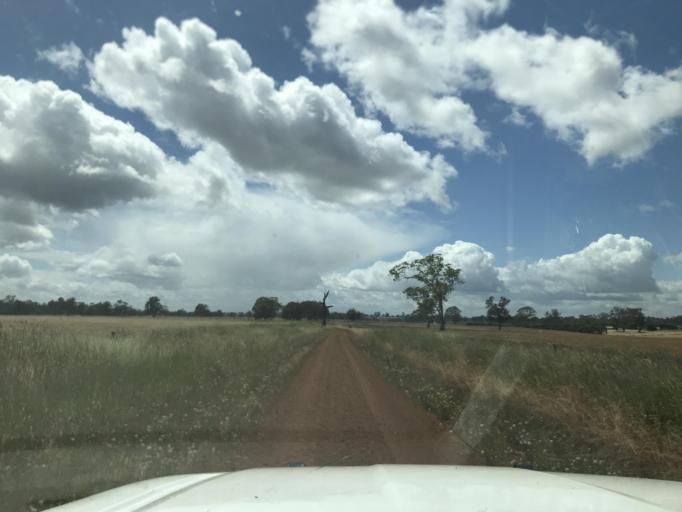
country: AU
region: South Australia
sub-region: Wattle Range
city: Penola
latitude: -37.1835
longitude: 141.4640
